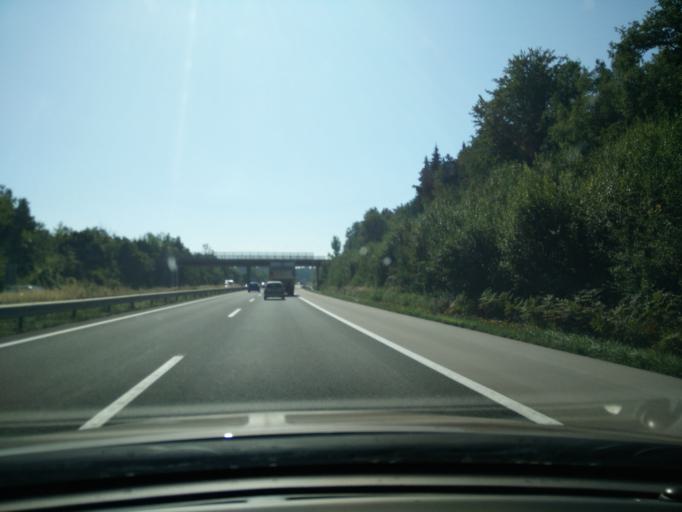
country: SI
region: Kranj
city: Britof
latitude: 46.2537
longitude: 14.3844
